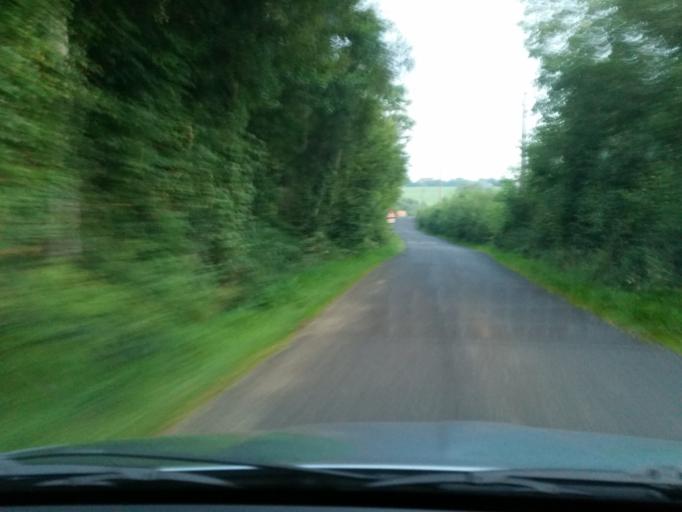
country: GB
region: Northern Ireland
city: Fivemiletown
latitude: 54.3156
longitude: -7.2955
